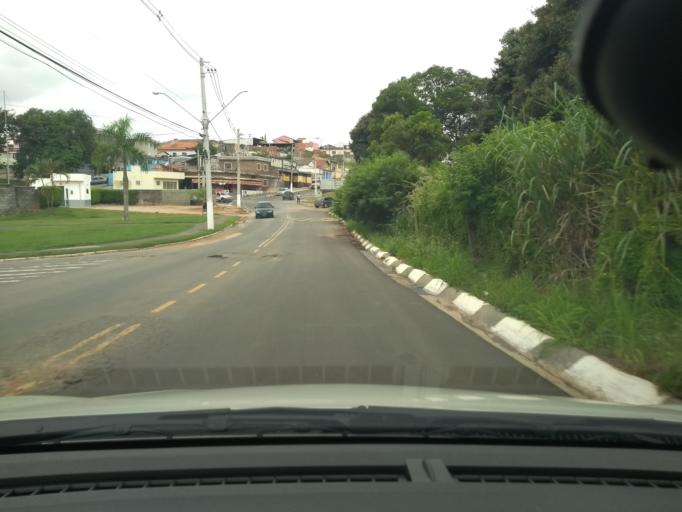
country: BR
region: Sao Paulo
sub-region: Itupeva
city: Itupeva
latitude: -23.1596
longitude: -47.0408
